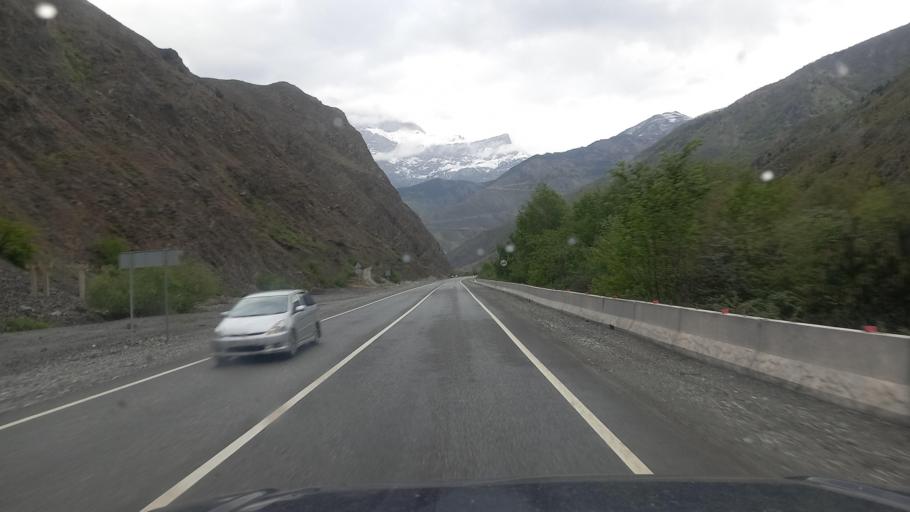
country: RU
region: North Ossetia
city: Mizur
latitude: 42.8573
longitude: 44.1126
